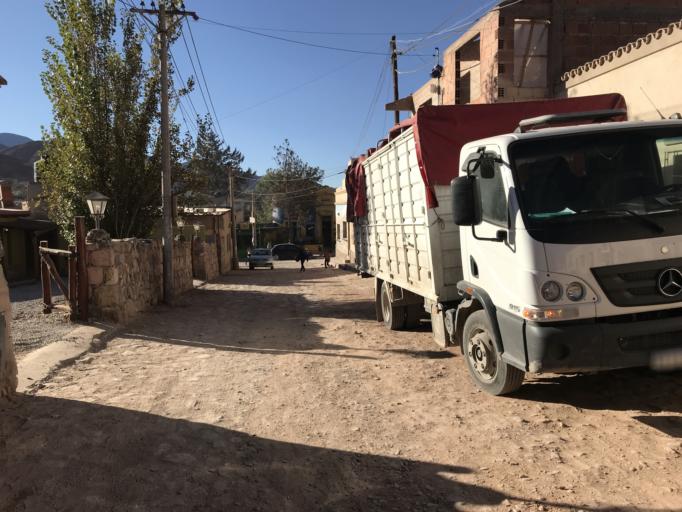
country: AR
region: Jujuy
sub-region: Departamento de Tilcara
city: Tilcara
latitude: -23.5772
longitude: -65.3959
